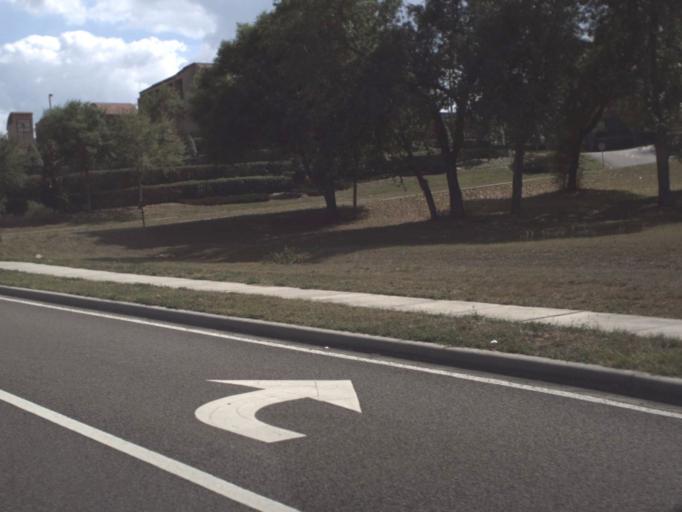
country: US
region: Florida
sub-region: Lake County
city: Clermont
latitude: 28.5390
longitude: -81.7392
